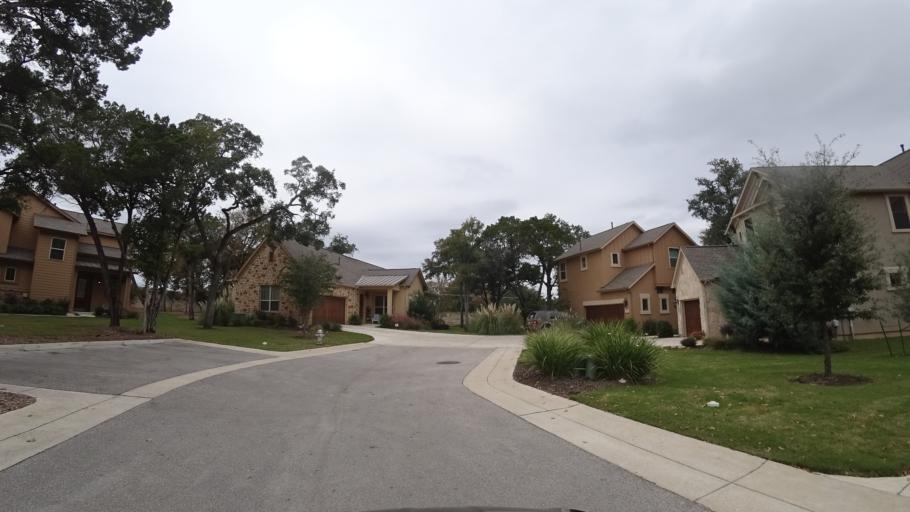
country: US
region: Texas
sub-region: Travis County
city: Shady Hollow
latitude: 30.1487
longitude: -97.8522
